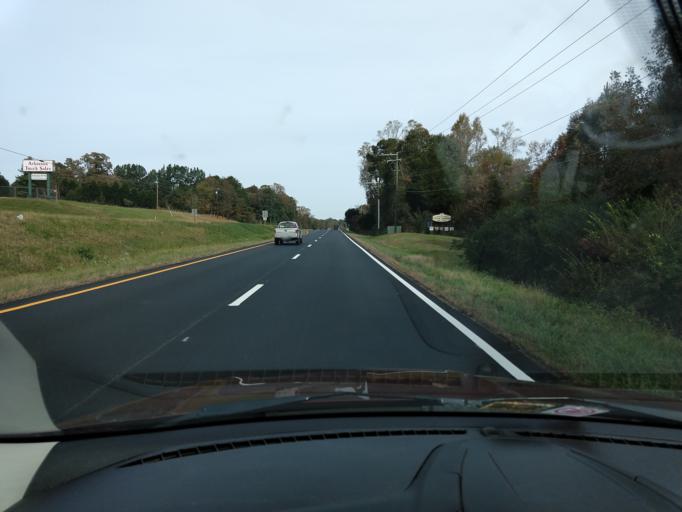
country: US
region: Virginia
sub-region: Pittsylvania County
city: Chatham
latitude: 36.7962
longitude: -79.3935
